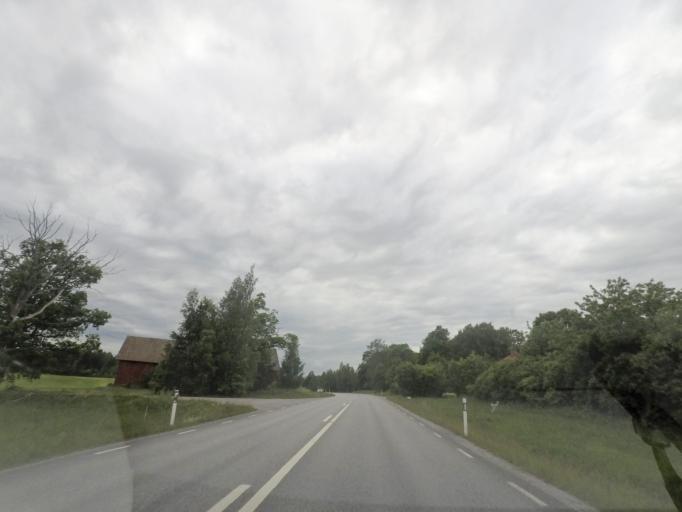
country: SE
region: Vaestmanland
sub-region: Arboga Kommun
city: Arboga
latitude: 59.4121
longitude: 15.7866
